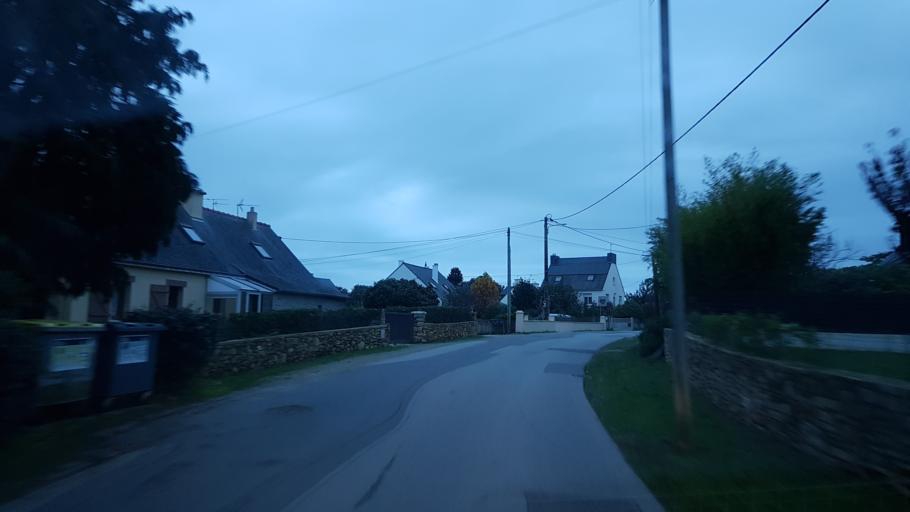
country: FR
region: Brittany
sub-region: Departement du Morbihan
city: Sarzeau
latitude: 47.5420
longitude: -2.7859
